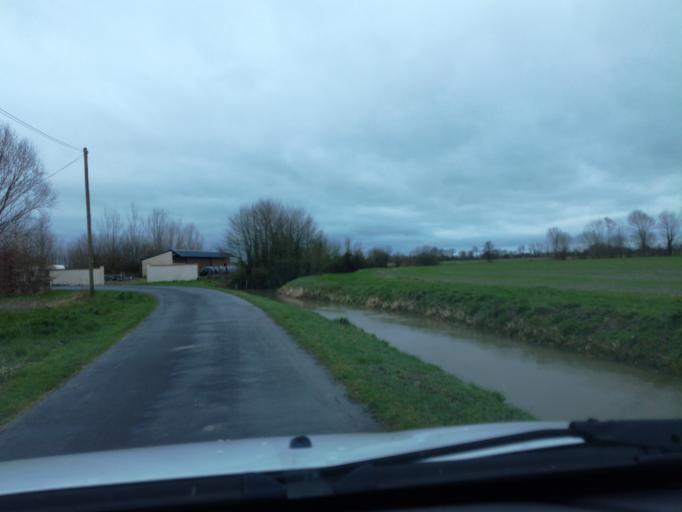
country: FR
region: Brittany
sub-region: Departement d'Ille-et-Vilaine
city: Cherrueix
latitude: 48.5799
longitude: -1.7129
